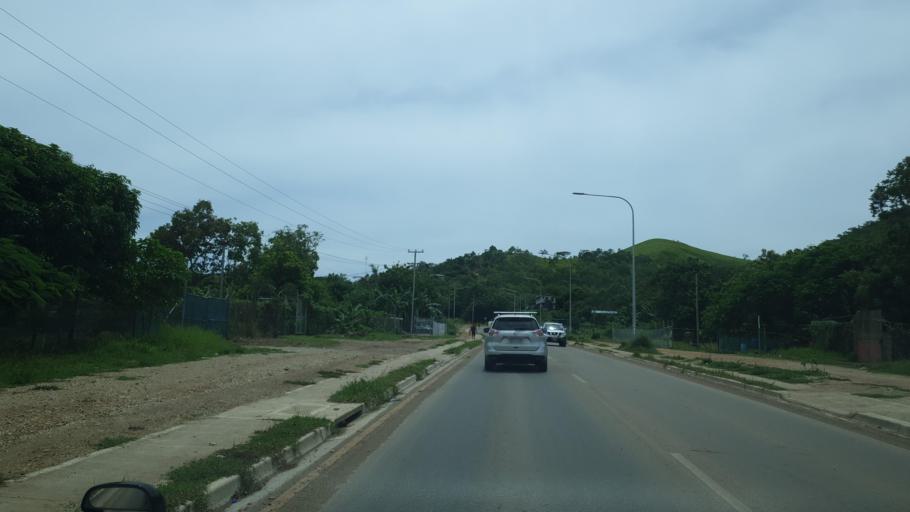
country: PG
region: National Capital
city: Port Moresby
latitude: -9.5145
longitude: 147.2409
